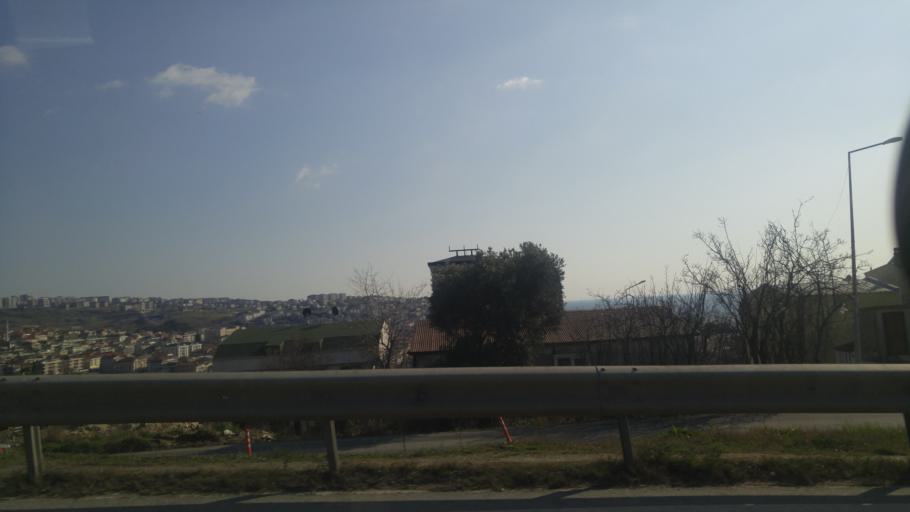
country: TR
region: Istanbul
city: Bueyuekcekmece
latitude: 41.0236
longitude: 28.5989
